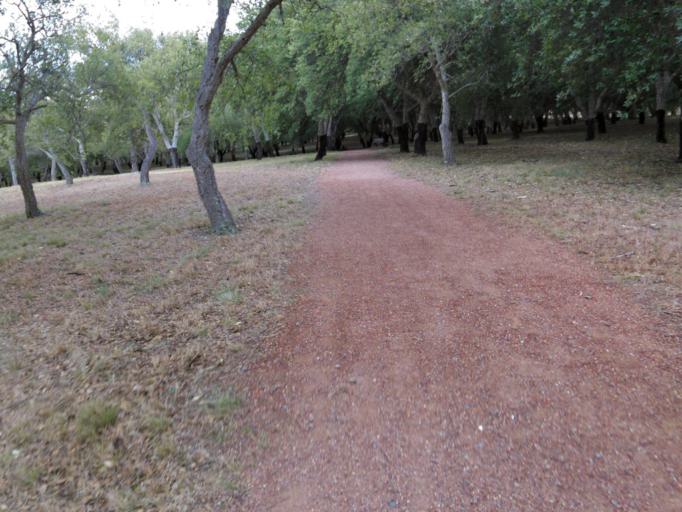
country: AU
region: Australian Capital Territory
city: Macquarie
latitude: -35.2810
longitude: 149.0807
